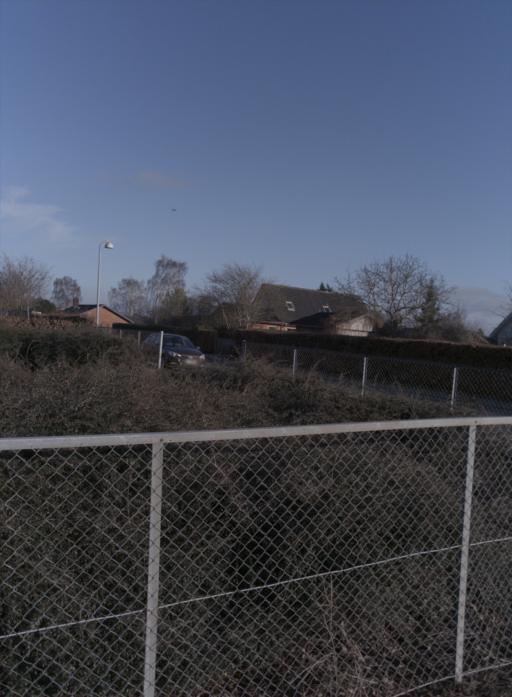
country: DK
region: Zealand
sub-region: Kalundborg Kommune
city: Kalundborg
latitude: 55.6902
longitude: 11.1486
